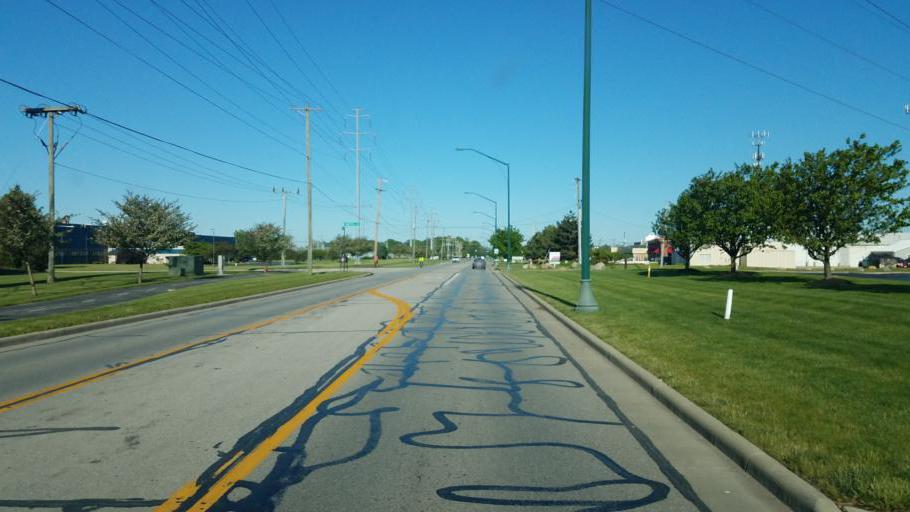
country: US
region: Ohio
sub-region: Franklin County
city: Westerville
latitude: 40.1463
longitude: -82.9145
